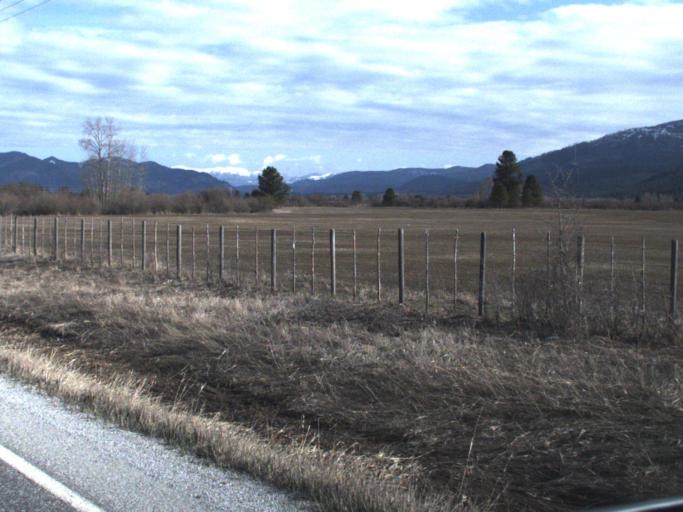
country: US
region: Washington
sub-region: Pend Oreille County
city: Newport
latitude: 48.3788
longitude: -117.3071
